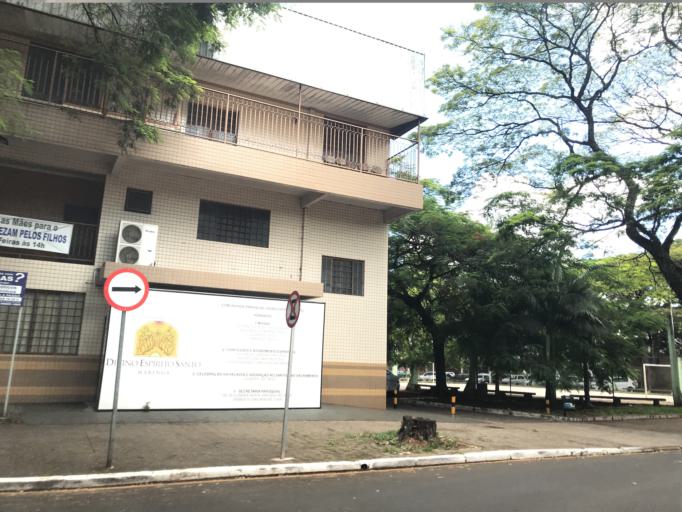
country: BR
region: Parana
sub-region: Maringa
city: Maringa
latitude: -23.4155
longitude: -51.9263
